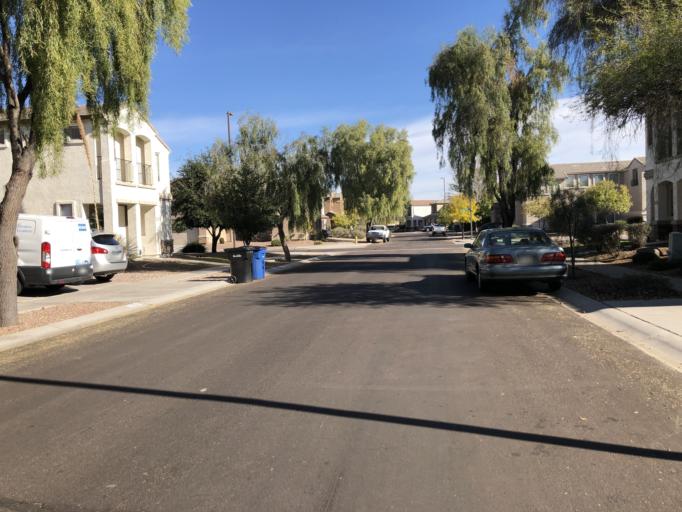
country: US
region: Arizona
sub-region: Maricopa County
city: Queen Creek
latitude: 33.2735
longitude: -111.7102
